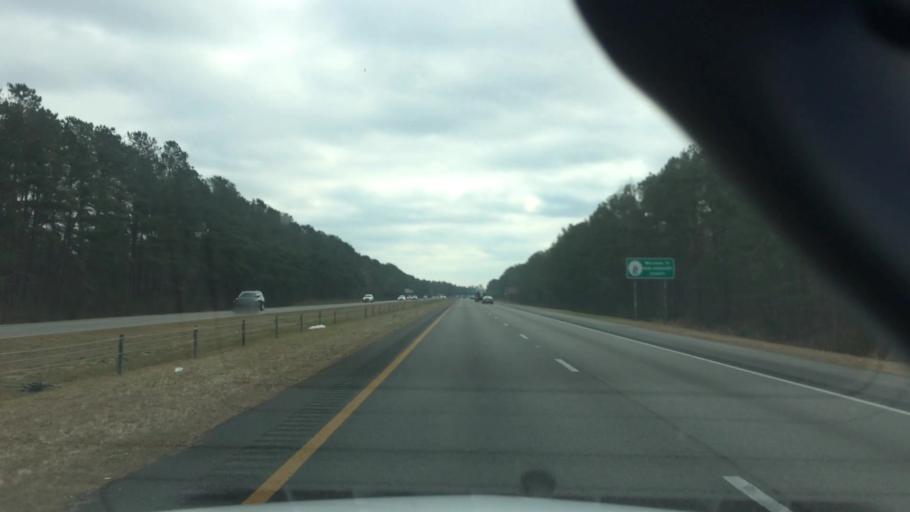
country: US
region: North Carolina
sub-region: New Hanover County
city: Skippers Corner
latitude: 34.3377
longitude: -77.8779
